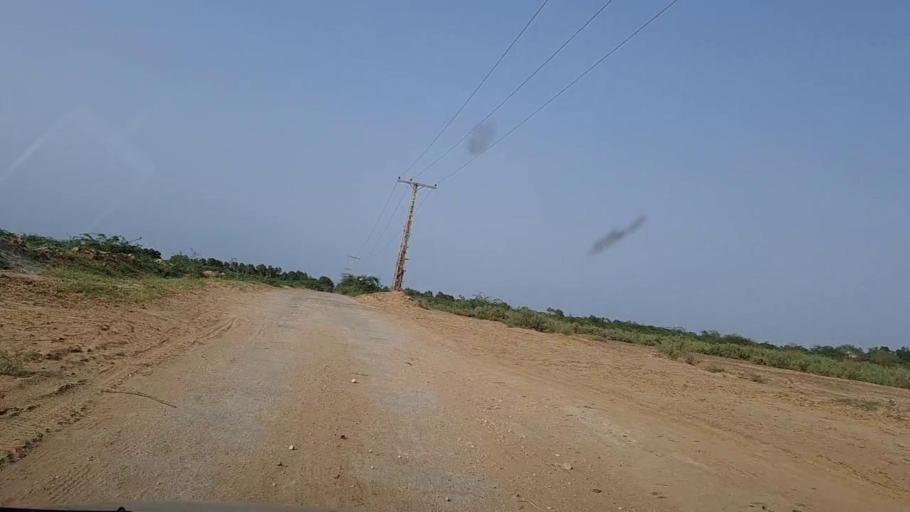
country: PK
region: Sindh
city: Kotri
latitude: 25.2215
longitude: 68.2472
